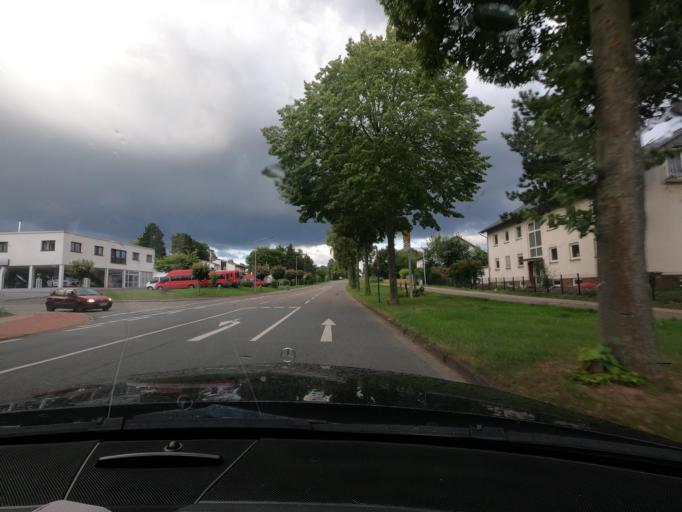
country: DE
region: Hesse
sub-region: Regierungsbezirk Kassel
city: Wolfhagen
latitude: 51.3203
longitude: 9.1837
